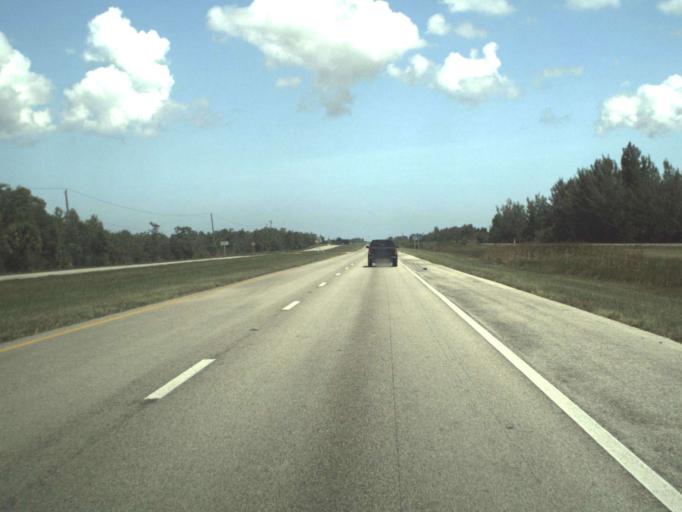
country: US
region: Florida
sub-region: Palm Beach County
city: Palm Beach Gardens
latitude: 26.8254
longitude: -80.1757
